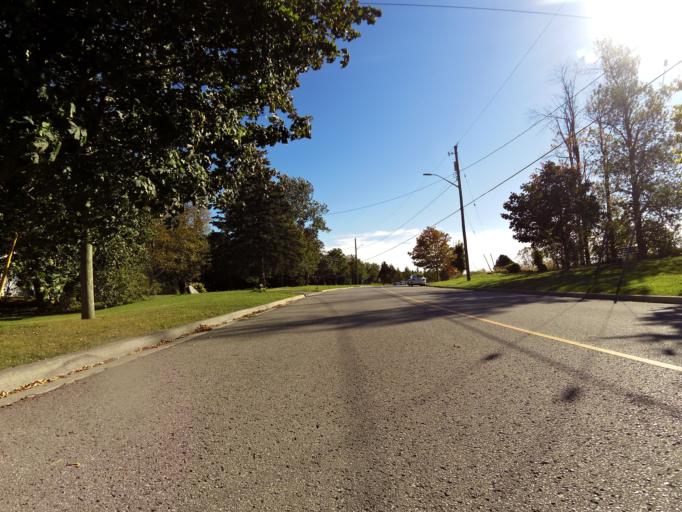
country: CA
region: Ontario
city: Oshawa
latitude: 43.8532
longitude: -78.8984
